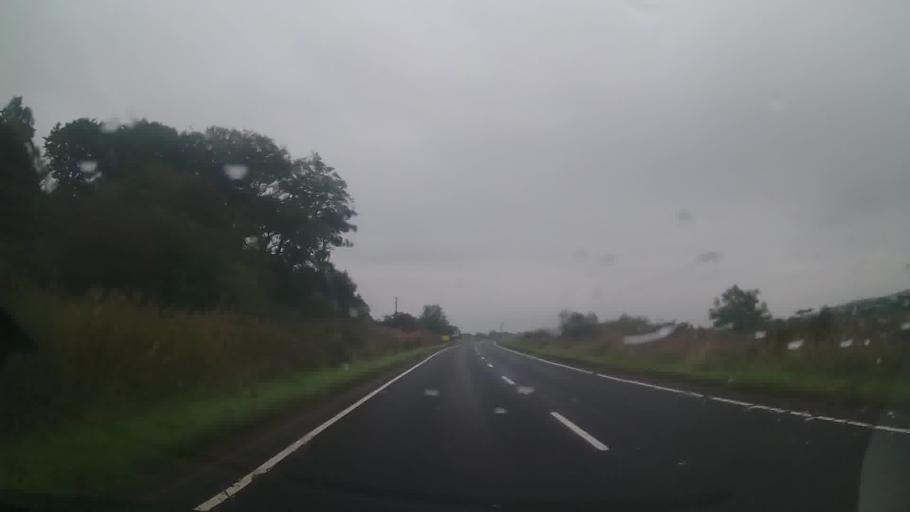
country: GB
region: Scotland
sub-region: North Ayrshire
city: Fairlie
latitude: 55.7196
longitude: -4.8625
